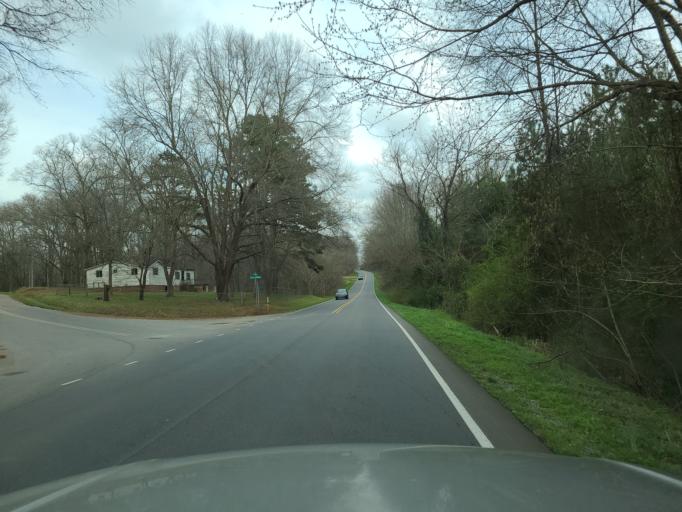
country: US
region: North Carolina
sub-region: Cleveland County
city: Boiling Springs
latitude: 35.2557
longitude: -81.6945
